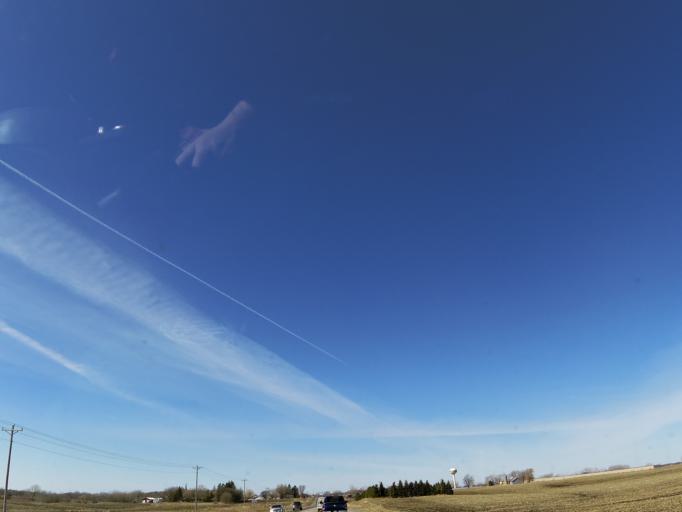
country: US
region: Minnesota
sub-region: Wright County
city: Rockford
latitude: 45.0798
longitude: -93.7086
